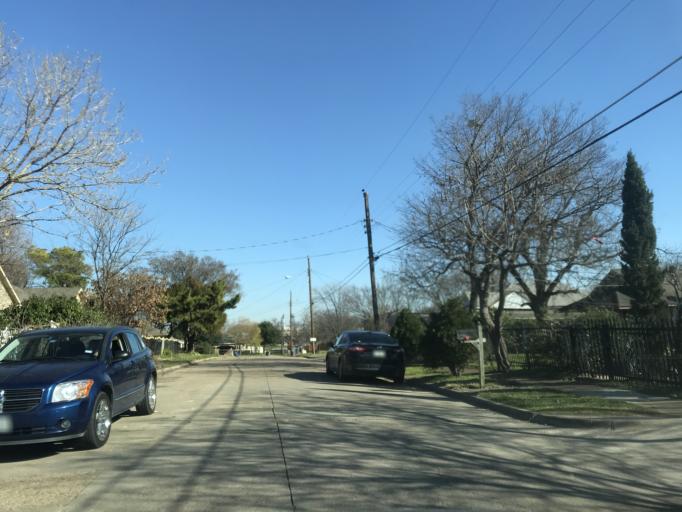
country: US
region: Texas
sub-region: Dallas County
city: Cockrell Hill
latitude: 32.7682
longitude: -96.9075
